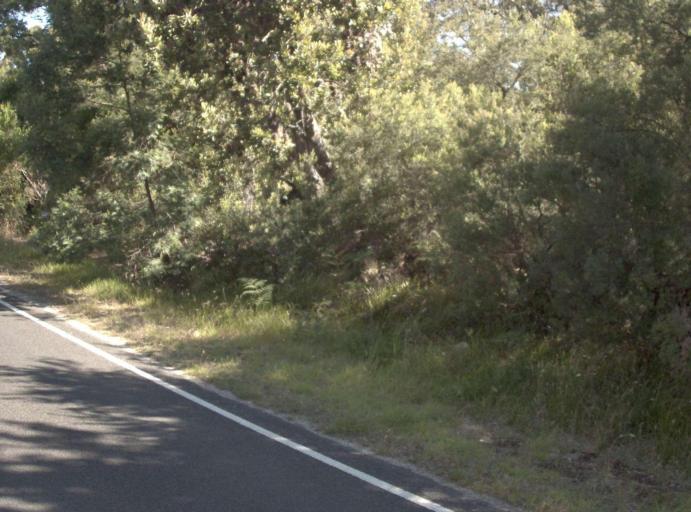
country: AU
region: Victoria
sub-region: Latrobe
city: Traralgon
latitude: -38.6572
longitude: 146.6801
